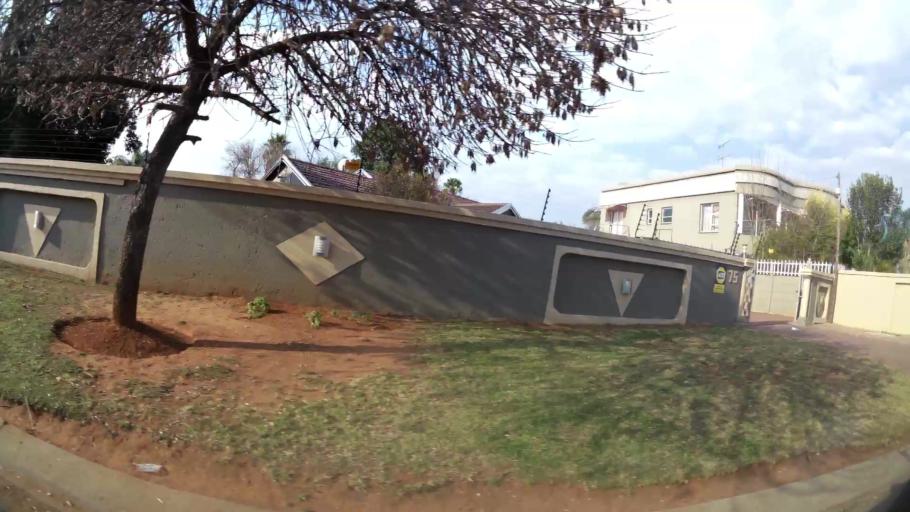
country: ZA
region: Gauteng
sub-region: Ekurhuleni Metropolitan Municipality
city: Benoni
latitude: -26.1229
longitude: 28.3716
